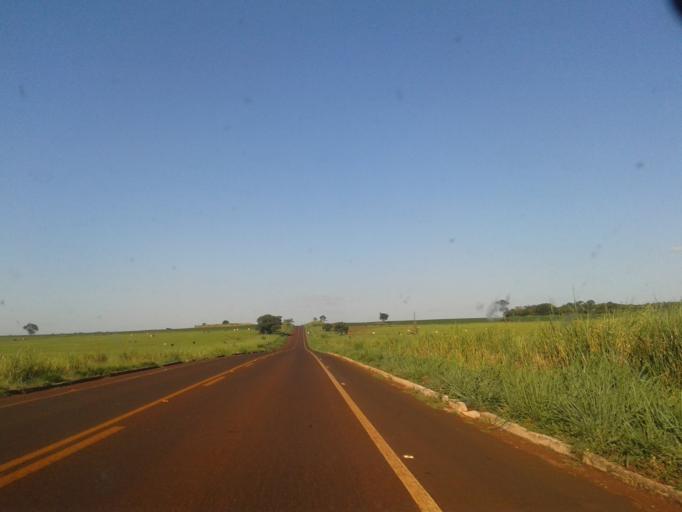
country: BR
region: Minas Gerais
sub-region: Capinopolis
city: Capinopolis
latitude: -18.7119
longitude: -49.7580
